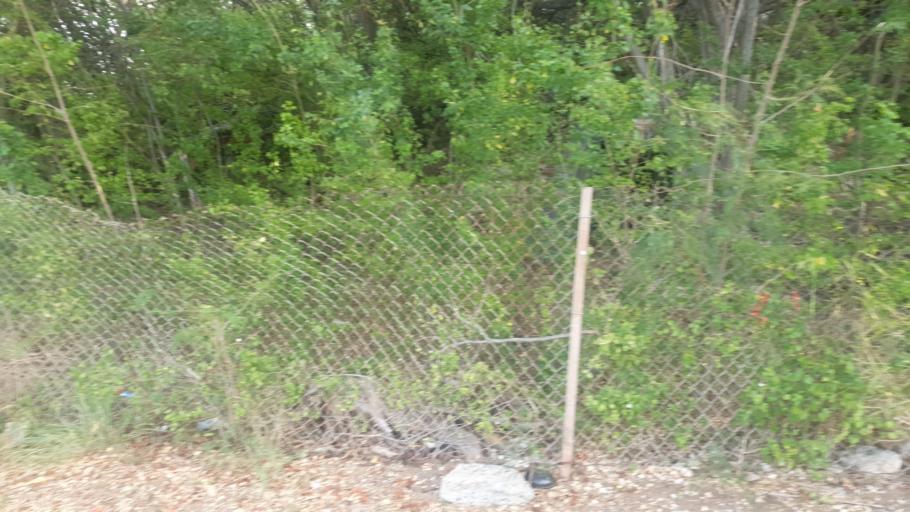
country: US
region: Hawaii
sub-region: Honolulu County
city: Iroquois Point
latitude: 21.3202
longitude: -157.9801
